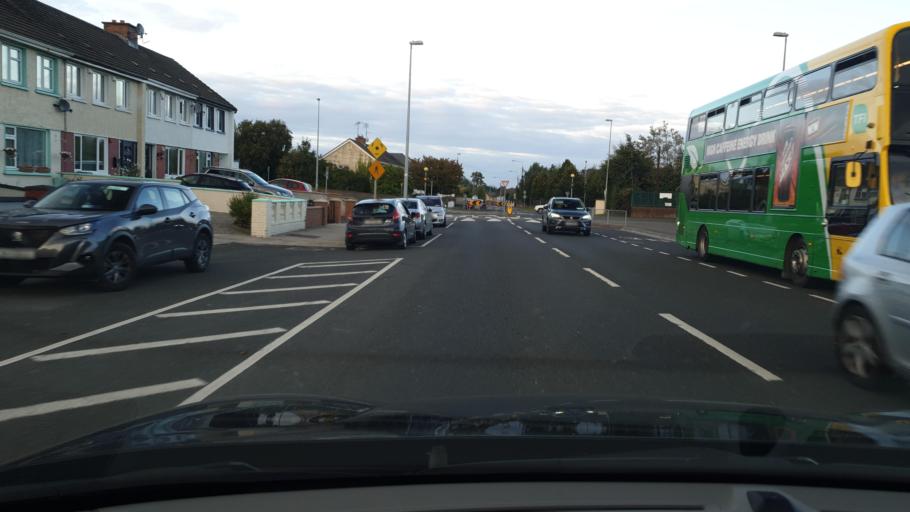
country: IE
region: Leinster
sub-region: South Dublin
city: Rathcoole
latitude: 53.2772
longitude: -6.4805
